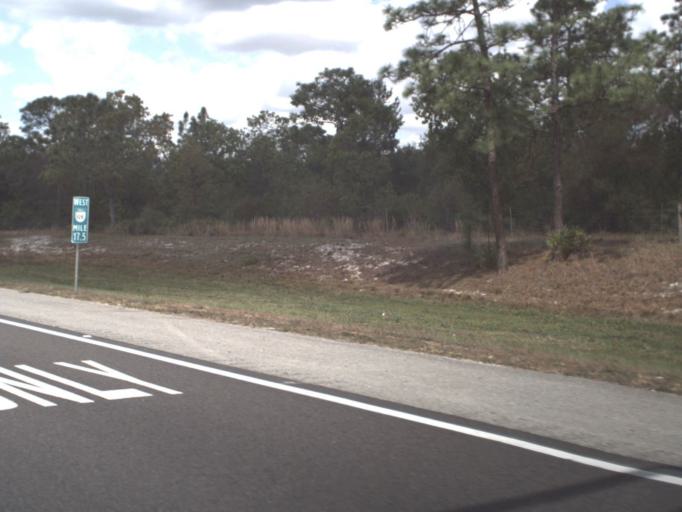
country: US
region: Florida
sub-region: Orange County
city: Alafaya
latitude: 28.4517
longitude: -81.1997
